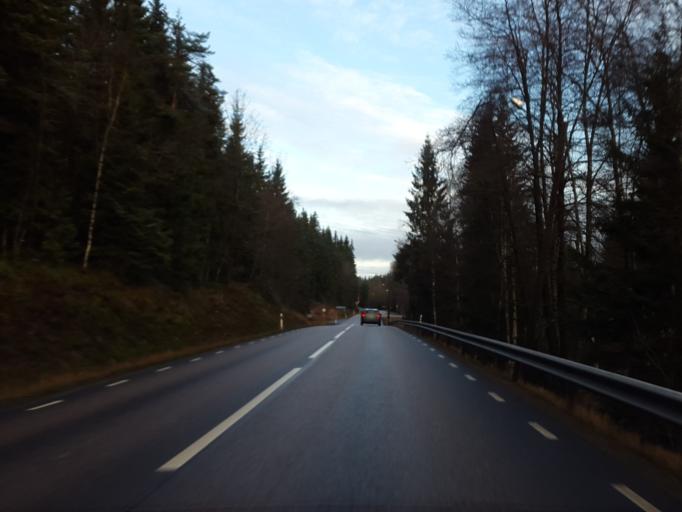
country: SE
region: Vaestra Goetaland
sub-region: Boras Kommun
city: Sjomarken
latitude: 57.7514
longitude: 12.8841
